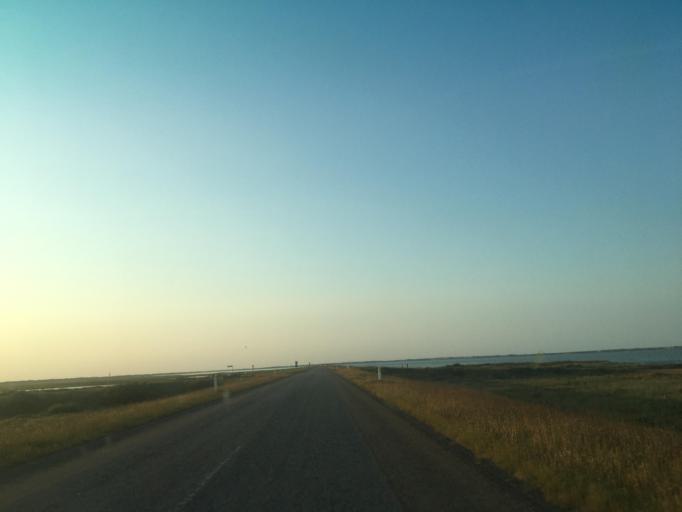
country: DK
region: Central Jutland
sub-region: Lemvig Kommune
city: Thyboron
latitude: 56.7224
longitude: 8.2492
